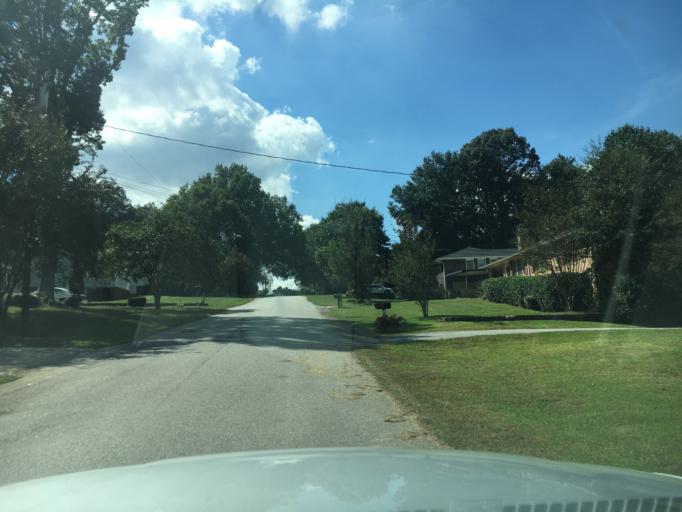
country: US
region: South Carolina
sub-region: Spartanburg County
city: Lyman
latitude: 34.9316
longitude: -82.1228
